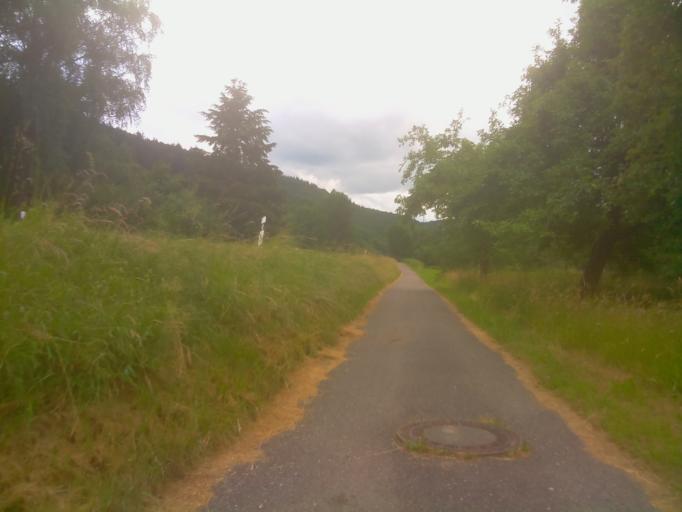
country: DE
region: Hesse
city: Neckarsteinach
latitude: 49.4097
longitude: 8.8719
